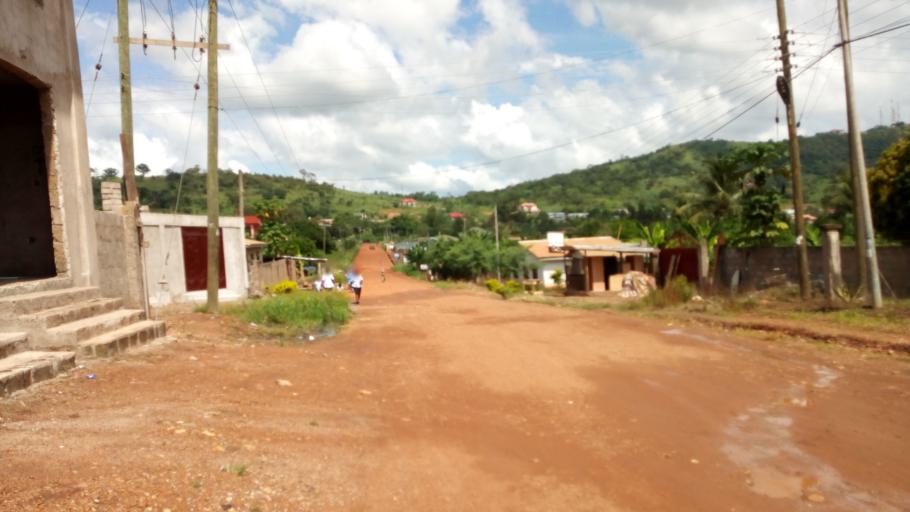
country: GH
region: Volta
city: Ho
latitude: 6.5916
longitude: 0.4413
